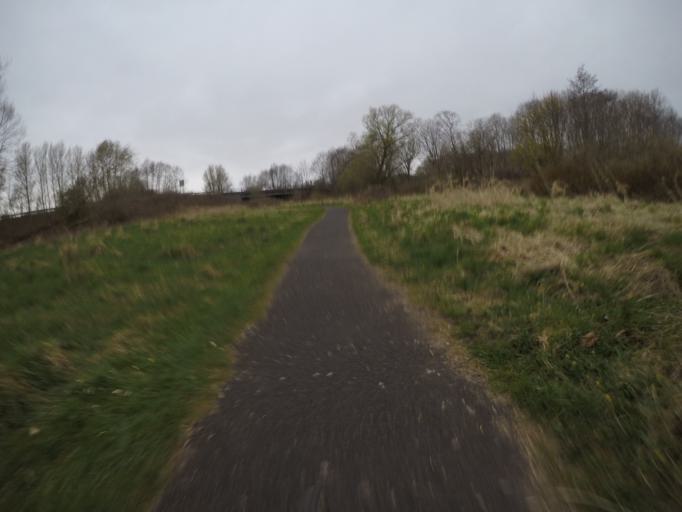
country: GB
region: Scotland
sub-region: North Ayrshire
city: Irvine
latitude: 55.6116
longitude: -4.6388
